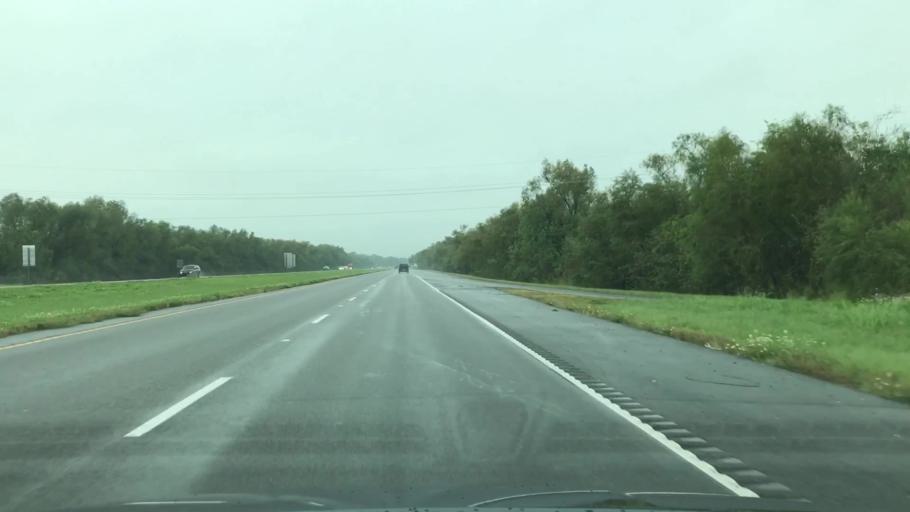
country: US
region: Louisiana
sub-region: Lafourche Parish
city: Raceland
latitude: 29.7047
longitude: -90.5755
